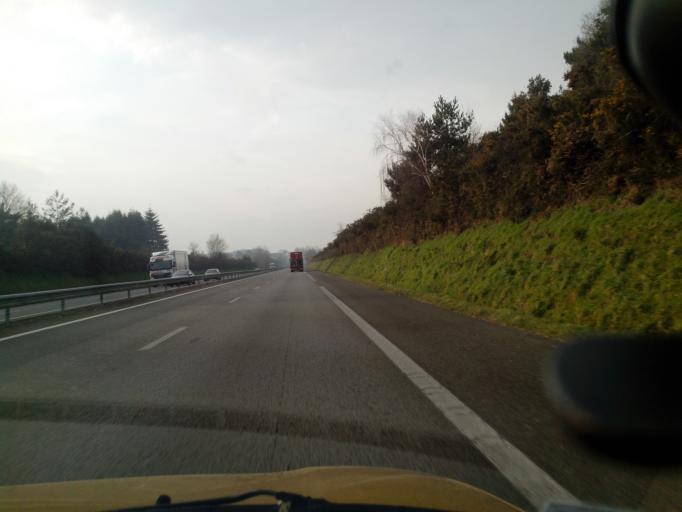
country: FR
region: Brittany
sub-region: Departement du Morbihan
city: Josselin
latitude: 47.9450
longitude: -2.5112
